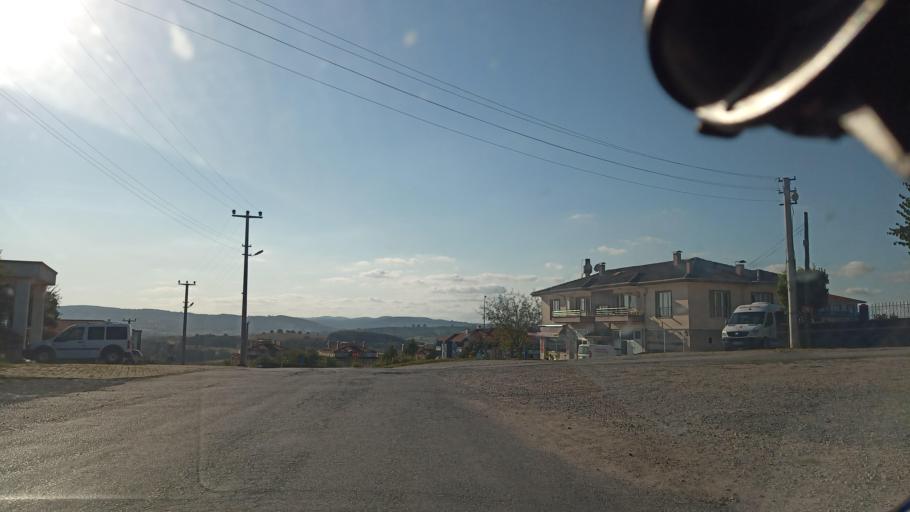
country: TR
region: Sakarya
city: Kazimpasa
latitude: 40.8511
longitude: 30.2802
